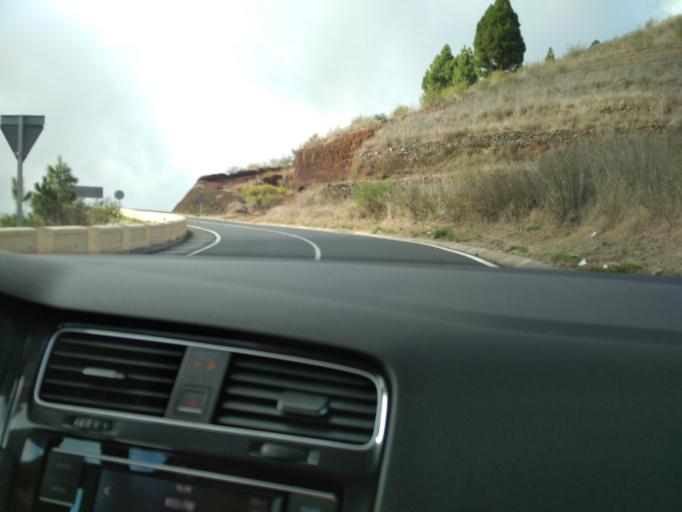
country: ES
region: Canary Islands
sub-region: Provincia de Santa Cruz de Tenerife
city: Santiago del Teide
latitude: 28.3192
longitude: -16.7963
